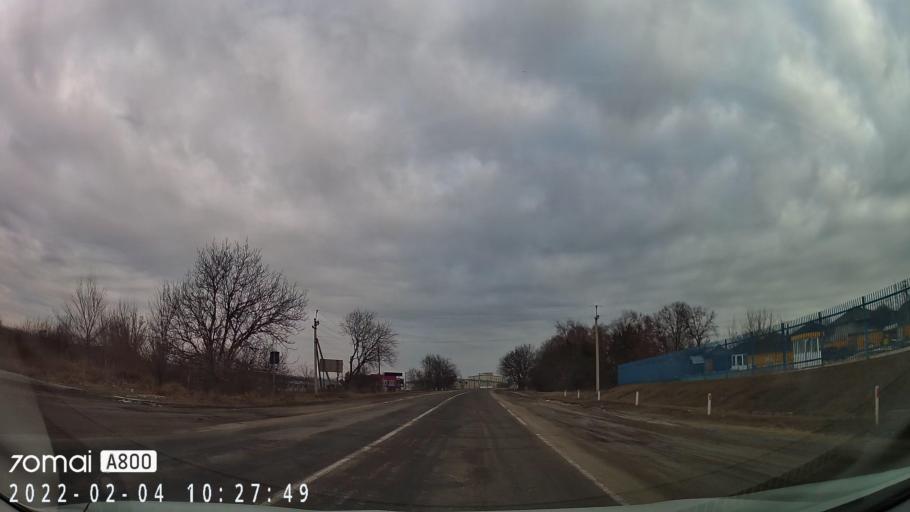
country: MD
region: Raionul Edinet
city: Edinet
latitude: 48.1734
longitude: 27.2796
